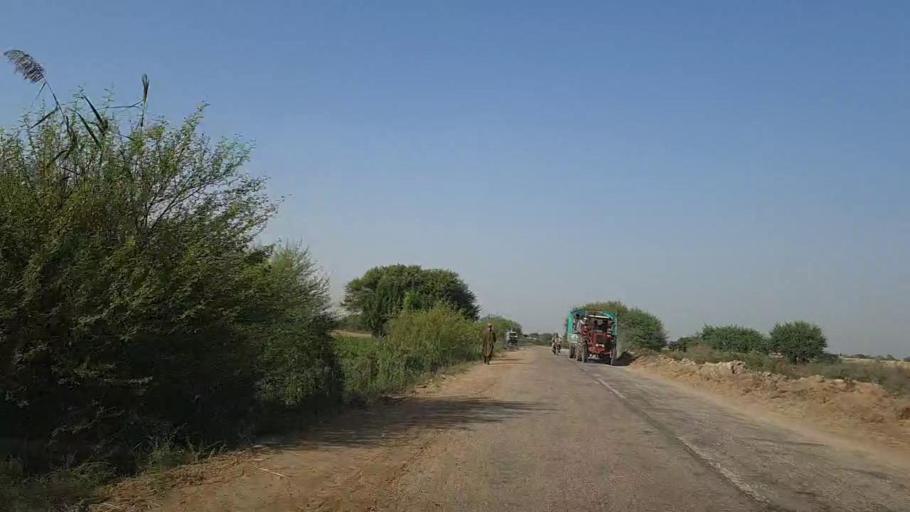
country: PK
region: Sindh
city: Mirpur Batoro
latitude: 24.5761
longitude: 68.3948
